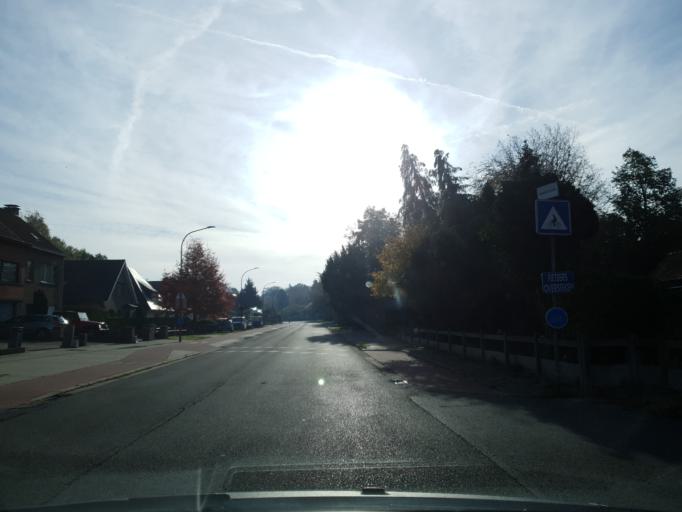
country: BE
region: Flanders
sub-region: Provincie Oost-Vlaanderen
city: Sint-Niklaas
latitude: 51.1540
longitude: 4.1678
